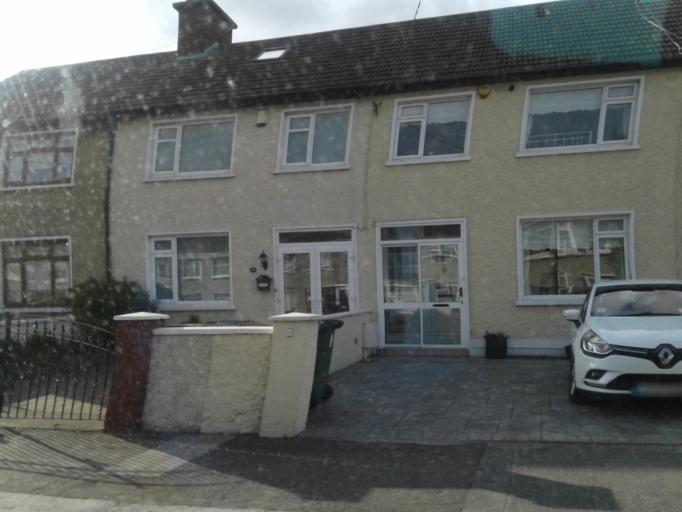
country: IE
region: Leinster
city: Artane
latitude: 53.3835
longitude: -6.2073
